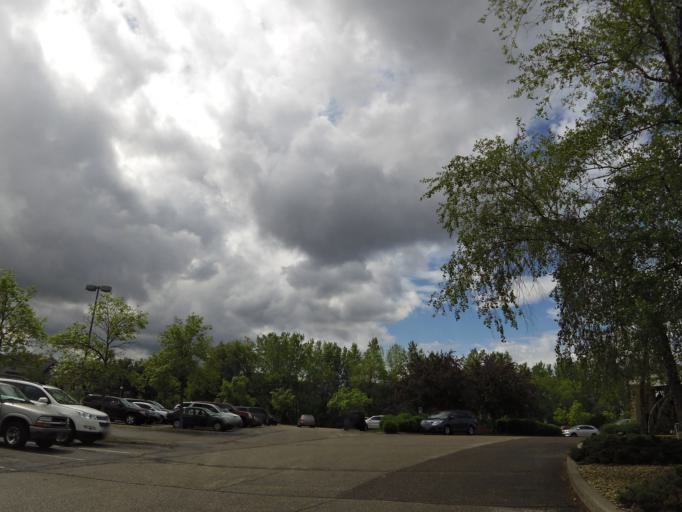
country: US
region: Wisconsin
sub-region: Saint Croix County
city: Hudson
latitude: 44.9772
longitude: -92.7351
